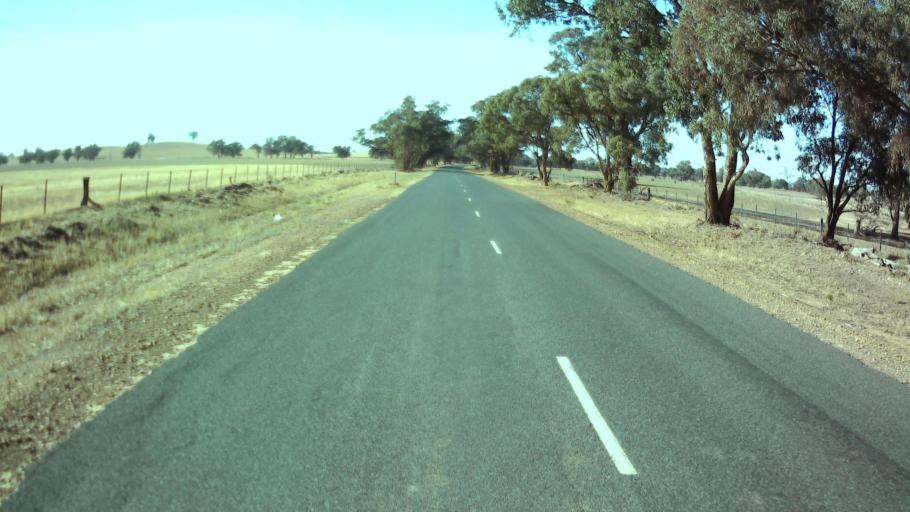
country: AU
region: New South Wales
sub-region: Weddin
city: Grenfell
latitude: -33.9547
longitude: 148.1391
